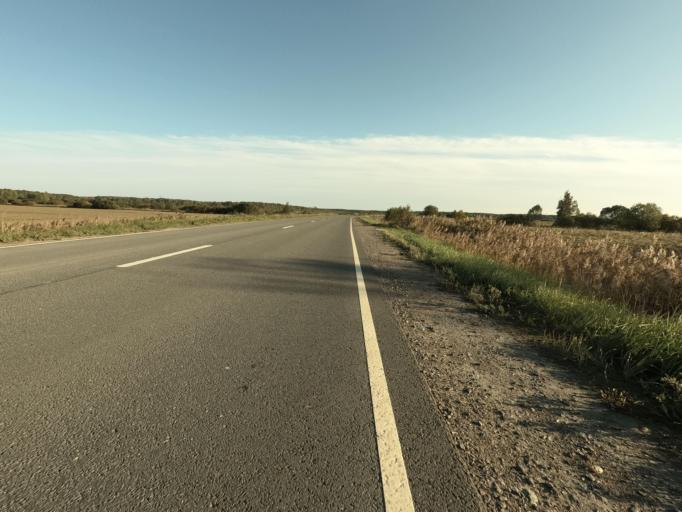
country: RU
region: St.-Petersburg
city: Sapernyy
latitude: 59.7430
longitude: 30.6484
